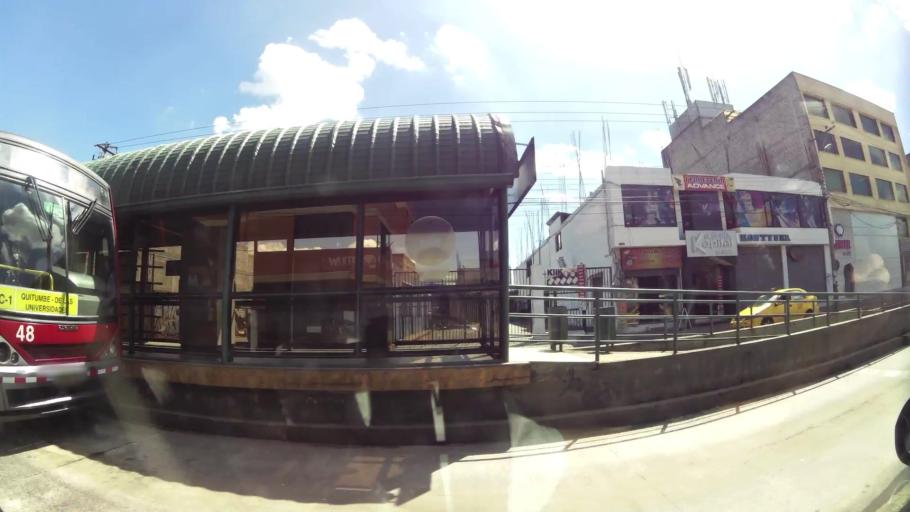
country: EC
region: Pichincha
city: Quito
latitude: -0.2988
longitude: -78.5467
